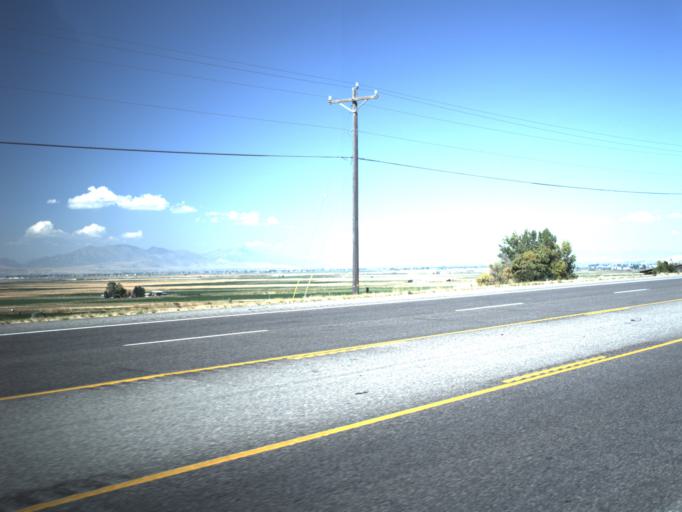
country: US
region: Utah
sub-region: Cache County
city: Smithfield
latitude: 41.8697
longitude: -111.8278
